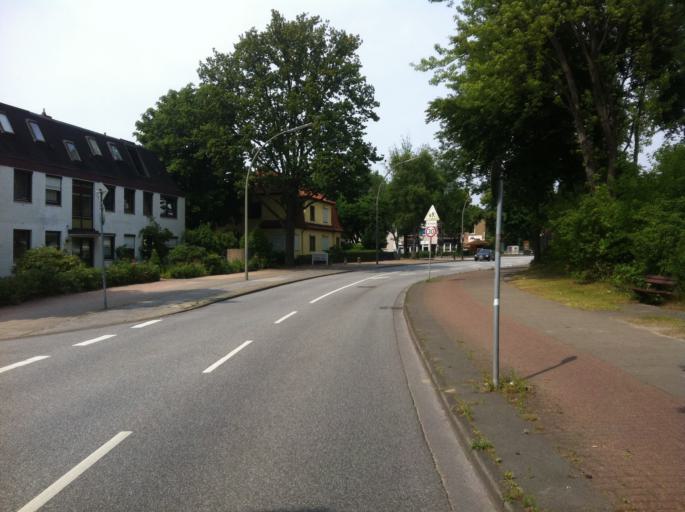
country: DE
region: Lower Saxony
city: Neu Wulmstorf
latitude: 53.4702
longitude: 9.8631
